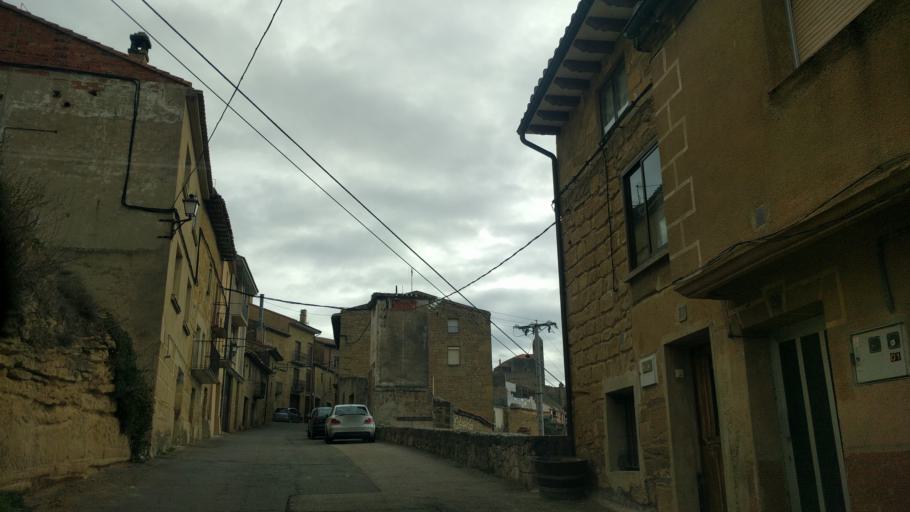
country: ES
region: La Rioja
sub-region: Provincia de La Rioja
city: San Vicente de la Sonsierra
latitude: 42.5625
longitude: -2.7604
